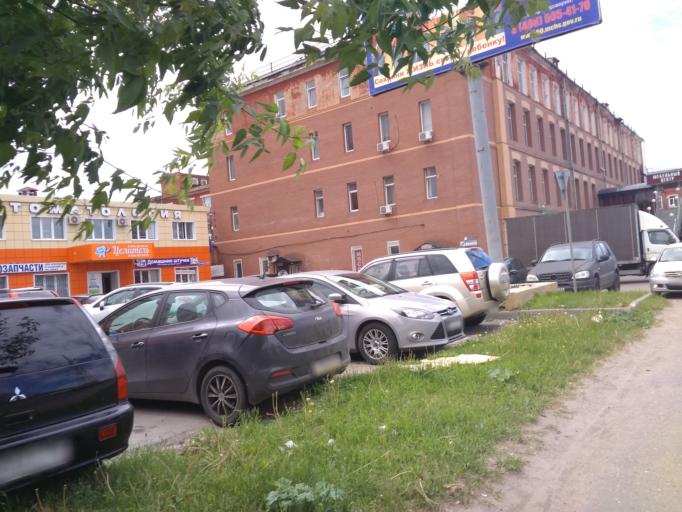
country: RU
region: Moskovskaya
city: Orekhovo-Zuyevo
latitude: 55.8046
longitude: 39.0021
